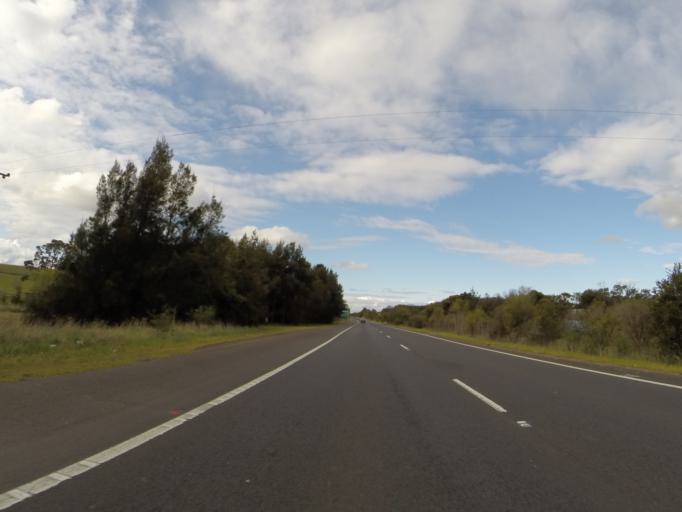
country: AU
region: New South Wales
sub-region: Wingecarribee
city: Bundanoon
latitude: -34.6051
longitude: 150.2301
